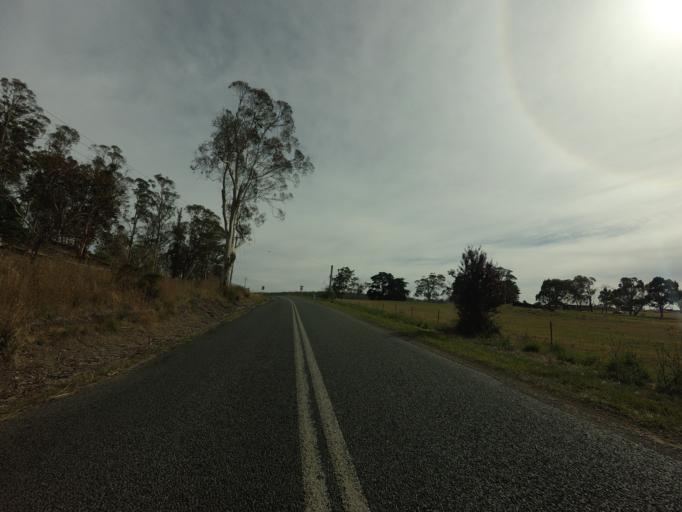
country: AU
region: Tasmania
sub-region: Brighton
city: Bridgewater
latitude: -42.3438
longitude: 147.4046
